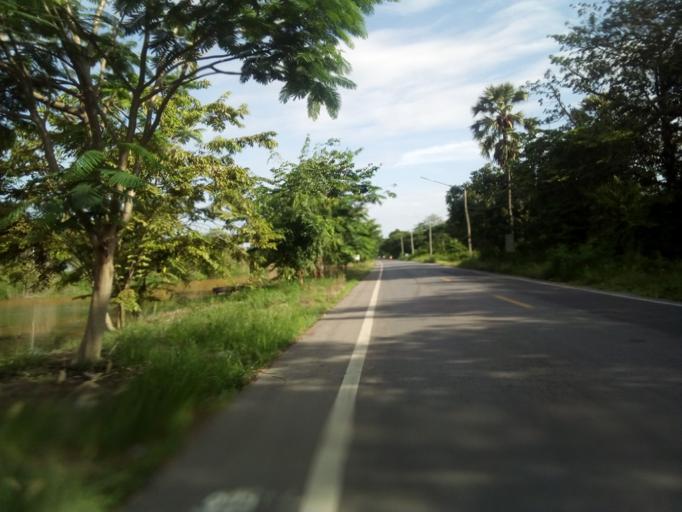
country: TH
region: Pathum Thani
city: Nong Suea
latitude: 14.1284
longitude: 100.8460
